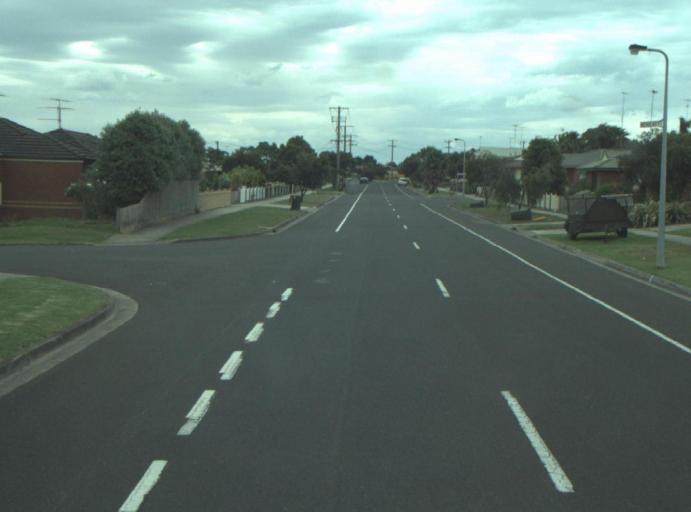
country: AU
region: Victoria
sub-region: Greater Geelong
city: Leopold
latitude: -38.1825
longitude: 144.4616
